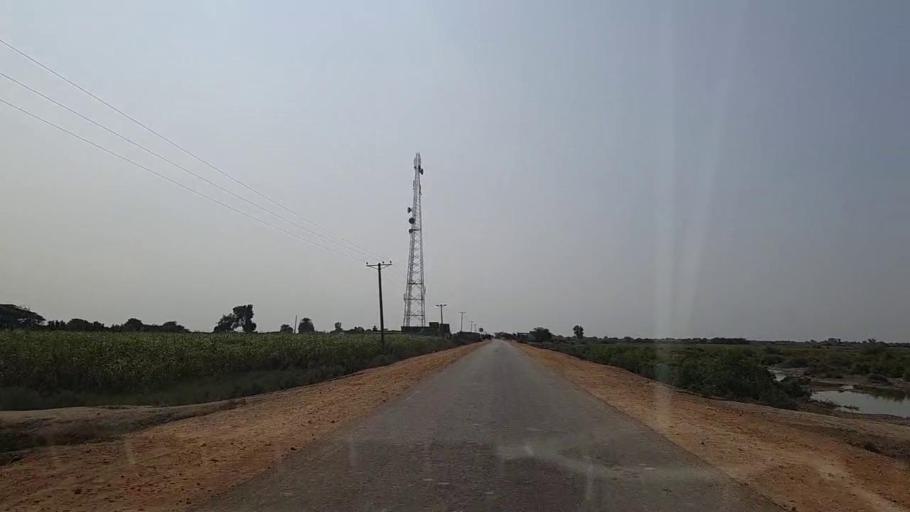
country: PK
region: Sindh
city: Chuhar Jamali
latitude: 24.2852
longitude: 67.9225
